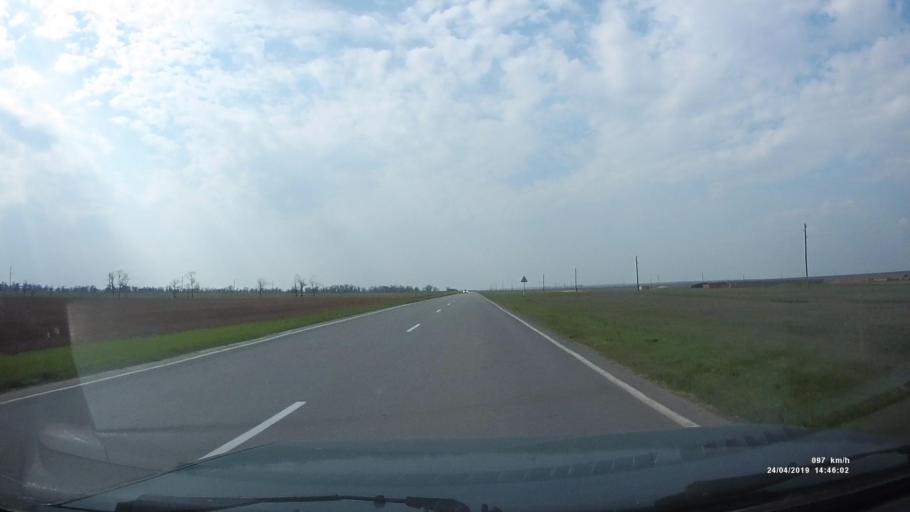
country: RU
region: Rostov
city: Remontnoye
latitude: 46.4781
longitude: 43.7970
